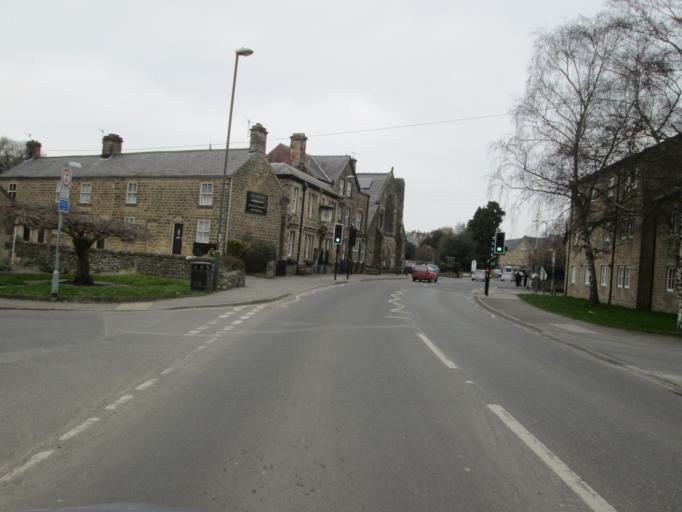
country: GB
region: England
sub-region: Derbyshire
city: Bakewell
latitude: 53.2108
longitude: -1.6737
